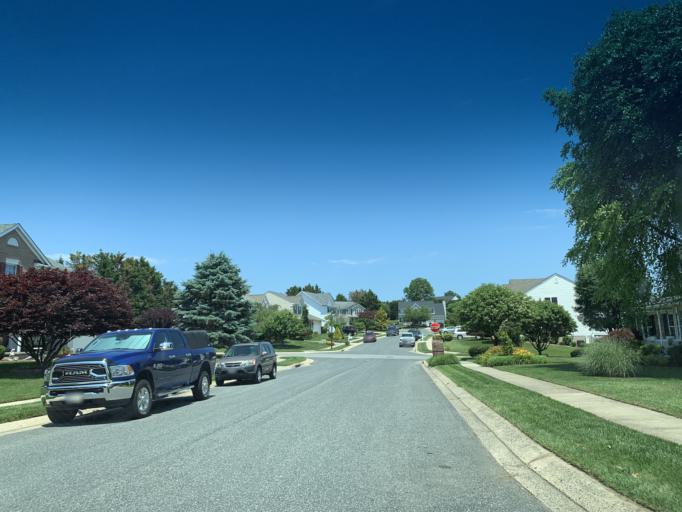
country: US
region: Maryland
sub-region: Harford County
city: Bel Air North
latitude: 39.5649
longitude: -76.3855
